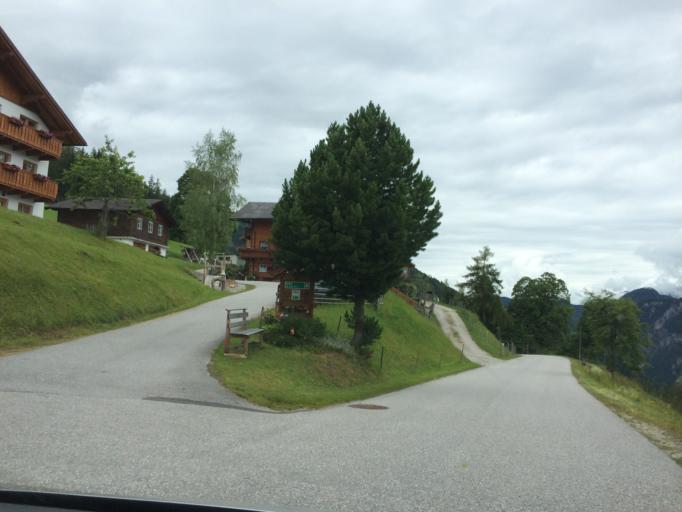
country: AT
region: Styria
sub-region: Politischer Bezirk Liezen
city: Schladming
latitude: 47.3790
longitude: 13.6290
